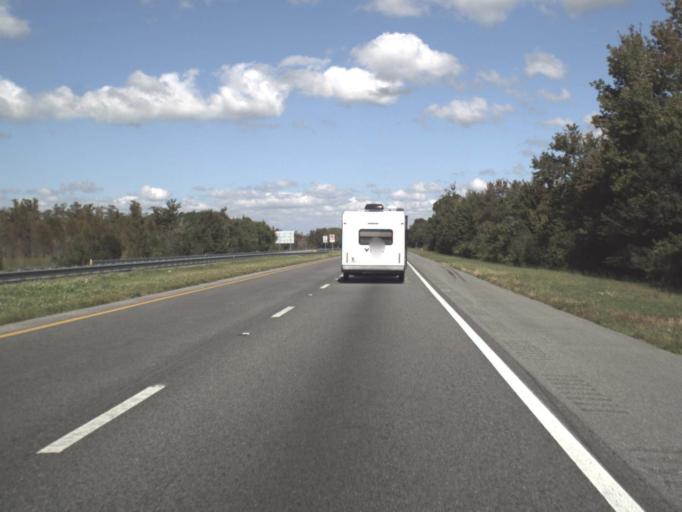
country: US
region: Florida
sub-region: Osceola County
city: Saint Cloud
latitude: 28.1398
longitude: -81.2927
